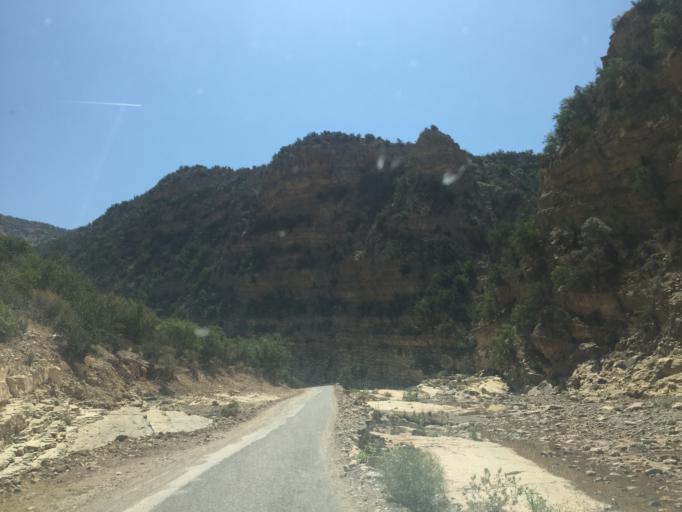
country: MA
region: Souss-Massa-Draa
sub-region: Agadir-Ida-ou-Tnan
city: Aourir
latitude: 30.5643
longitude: -9.5418
